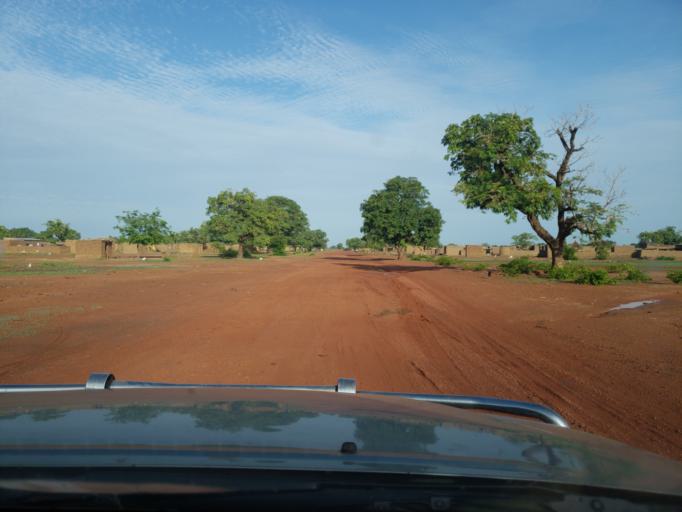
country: ML
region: Sikasso
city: Koutiala
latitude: 12.4294
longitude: -5.6122
